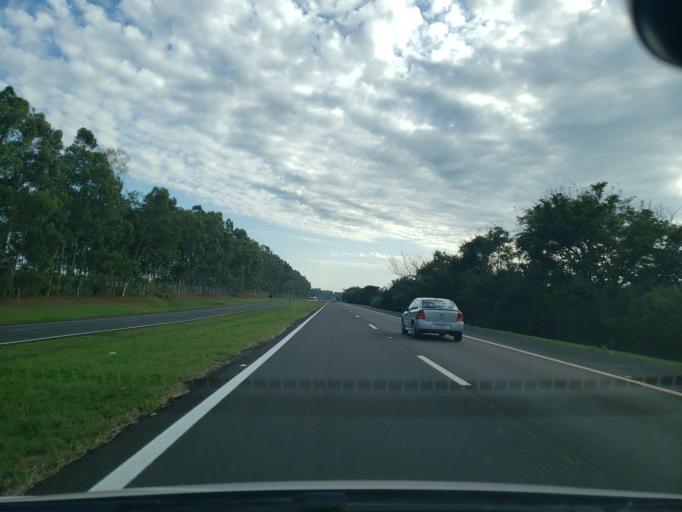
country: BR
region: Sao Paulo
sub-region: Guararapes
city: Guararapes
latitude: -21.2112
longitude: -50.6735
